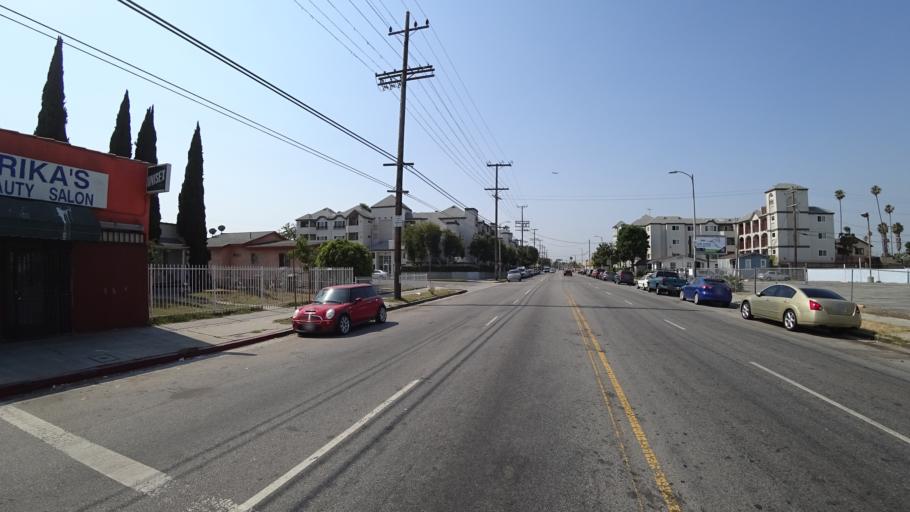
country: US
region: California
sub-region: Los Angeles County
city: Westmont
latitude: 33.9635
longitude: -118.2871
